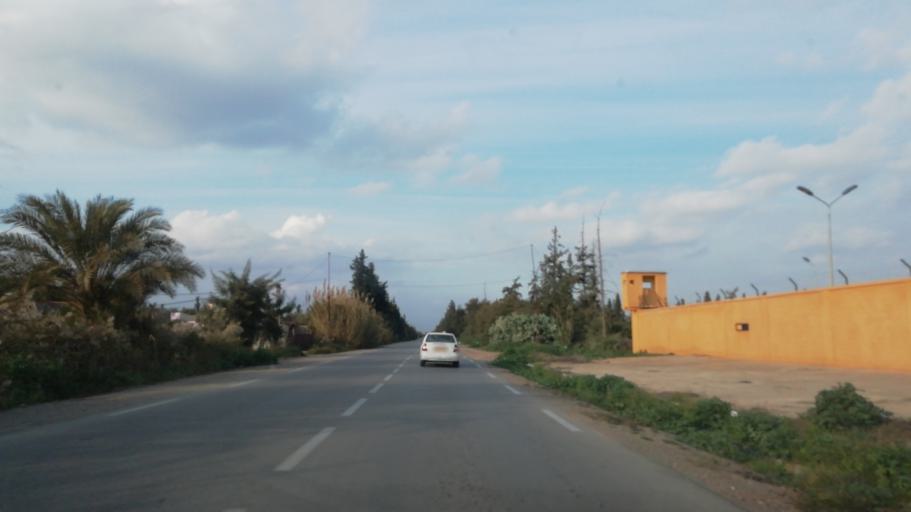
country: DZ
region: Mascara
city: Mascara
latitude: 35.6030
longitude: 0.0527
